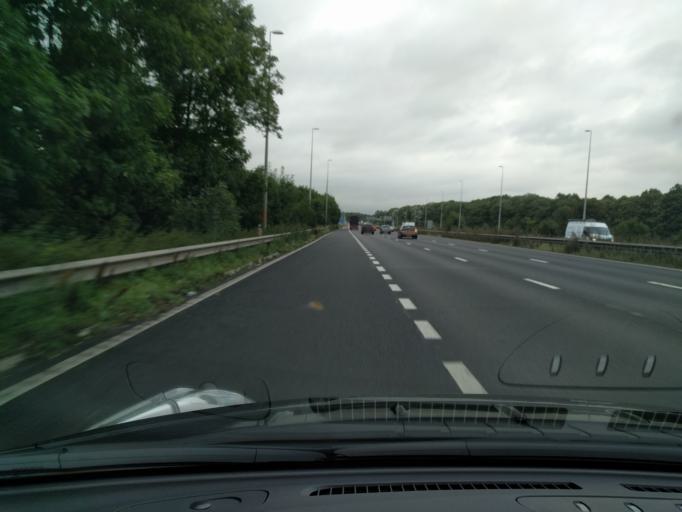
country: GB
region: England
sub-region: Warrington
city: Croft
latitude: 53.4285
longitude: -2.5469
